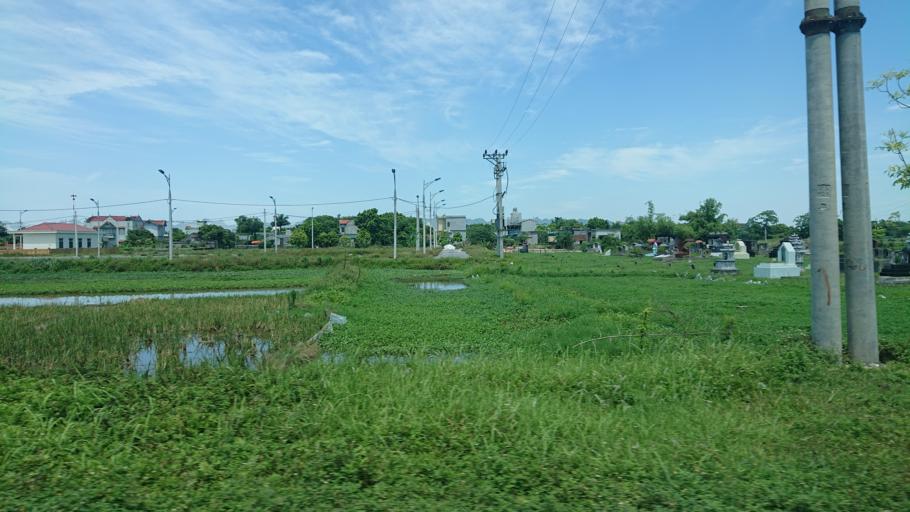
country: VN
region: Ha Nam
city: Thanh Pho Phu Ly
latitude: 20.5310
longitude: 105.9458
